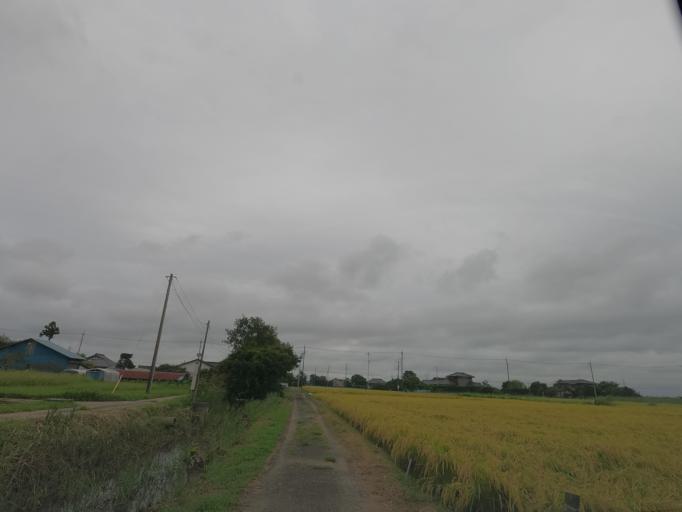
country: JP
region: Ibaraki
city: Toride
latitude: 35.9245
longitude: 140.0711
